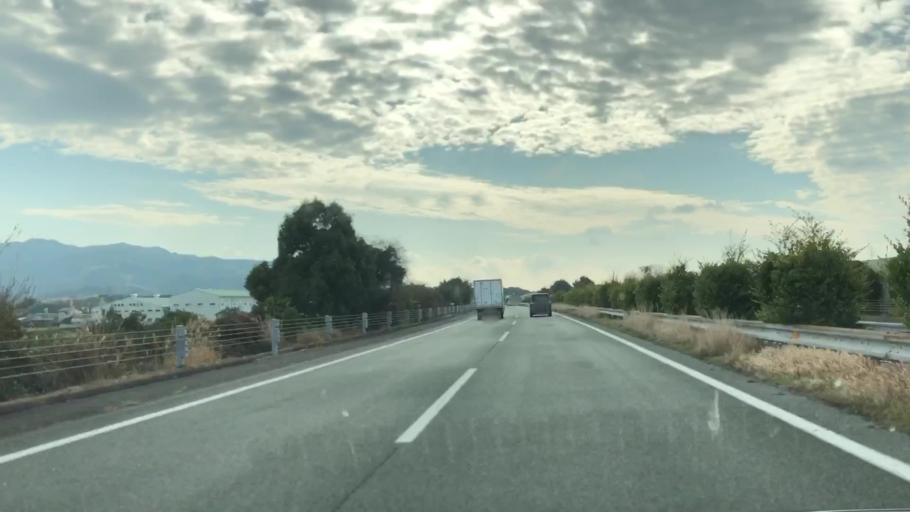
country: JP
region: Fukuoka
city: Setakamachi-takayanagi
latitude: 33.1901
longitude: 130.5201
